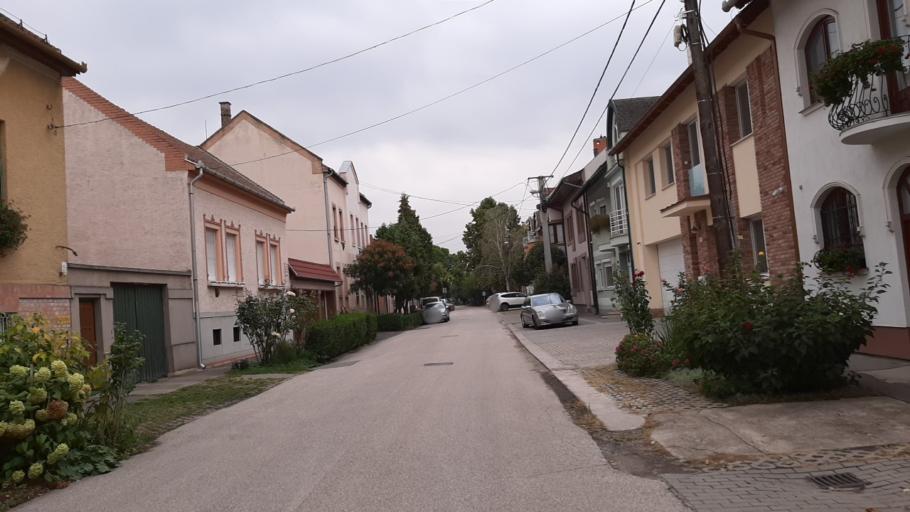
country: HU
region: Csongrad
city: Szeged
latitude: 46.2436
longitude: 20.1369
